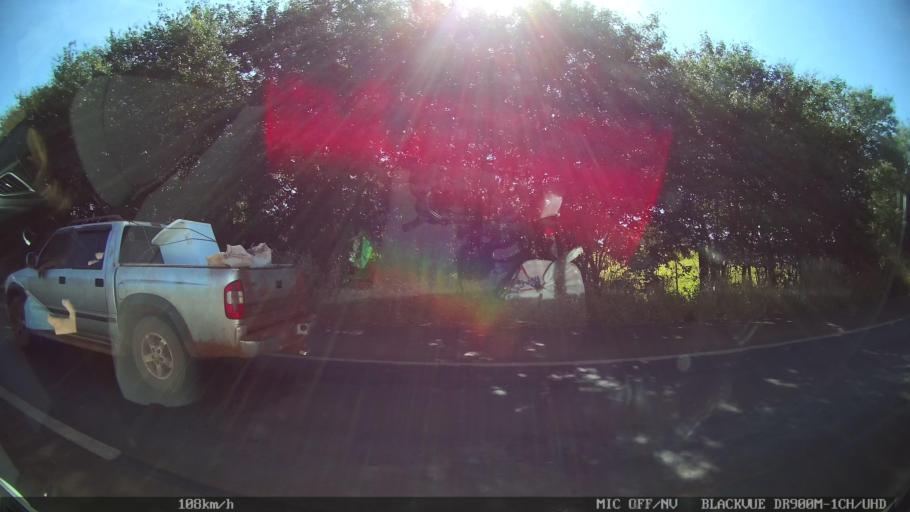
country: BR
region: Sao Paulo
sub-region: Barretos
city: Barretos
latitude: -20.5335
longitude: -48.6019
